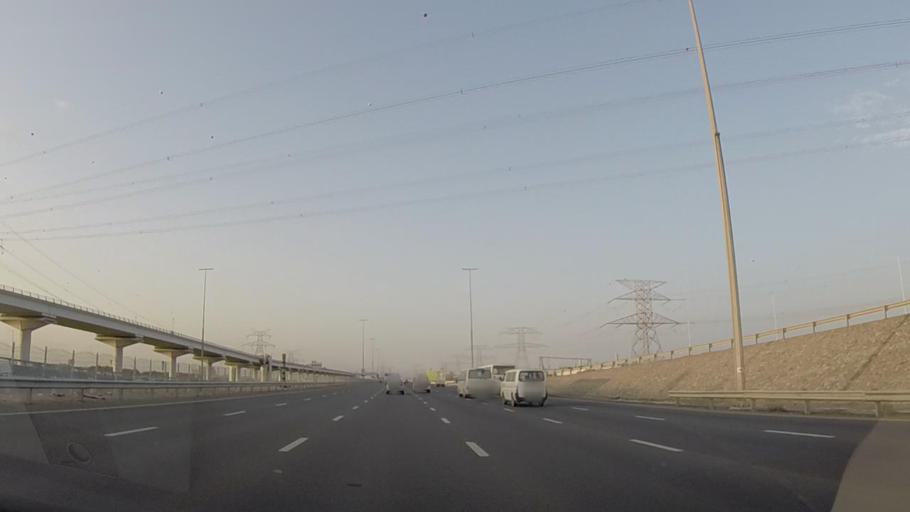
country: AE
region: Dubai
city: Dubai
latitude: 25.0329
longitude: 55.1046
